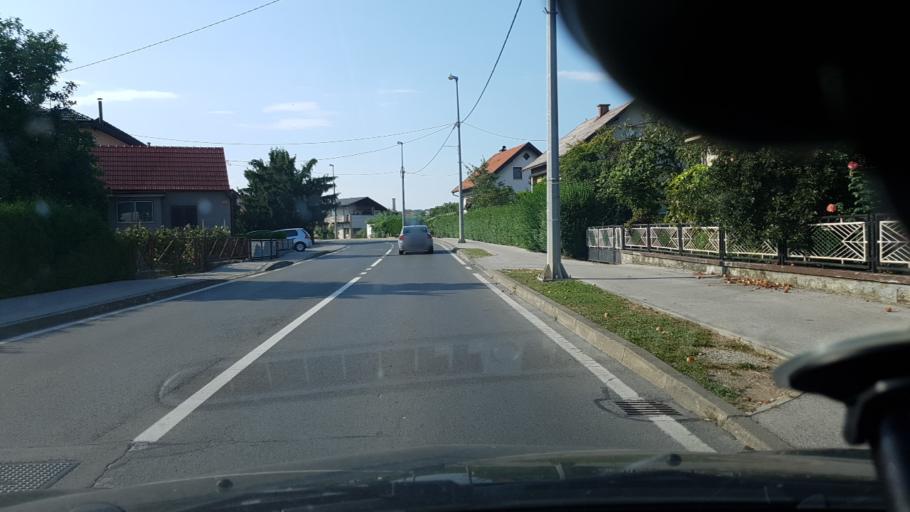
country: HR
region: Zagrebacka
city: Brdovec
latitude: 45.8614
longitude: 15.7948
